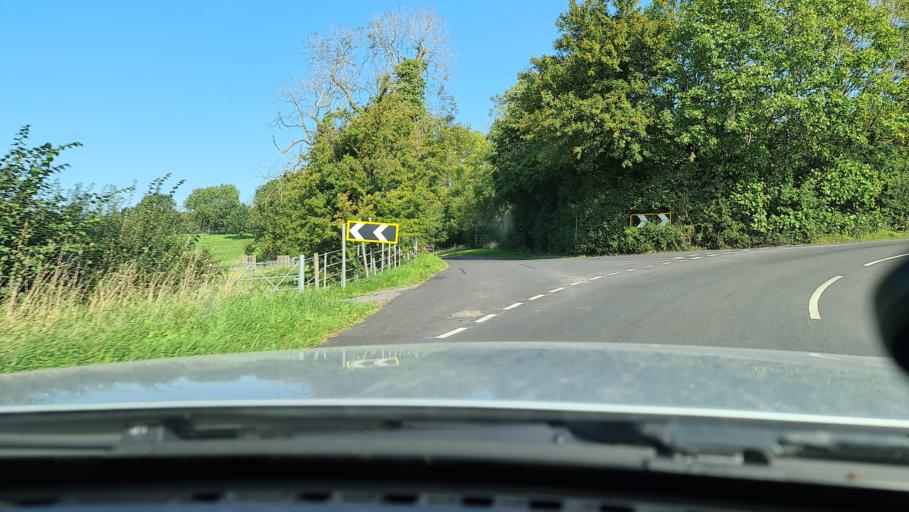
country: GB
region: England
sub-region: Northamptonshire
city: Daventry
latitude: 52.1489
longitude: -1.1591
